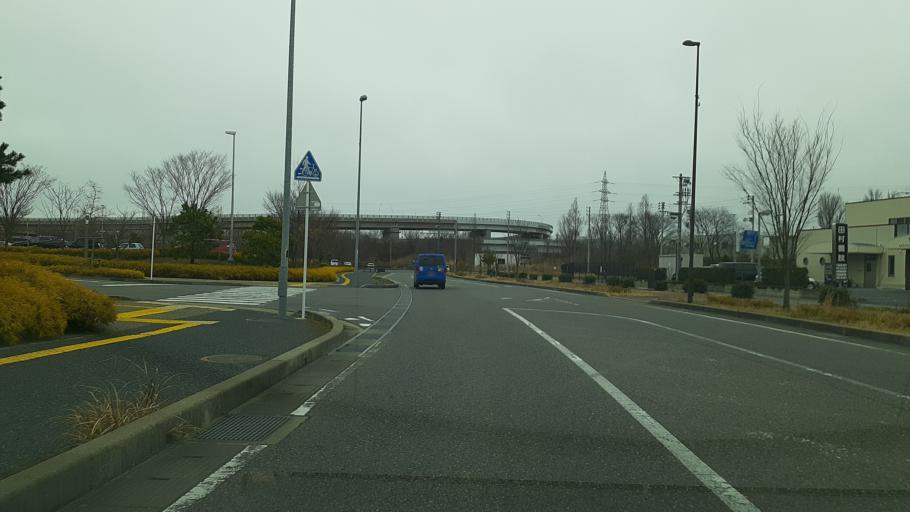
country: JP
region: Niigata
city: Niigata-shi
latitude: 37.8748
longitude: 139.0400
